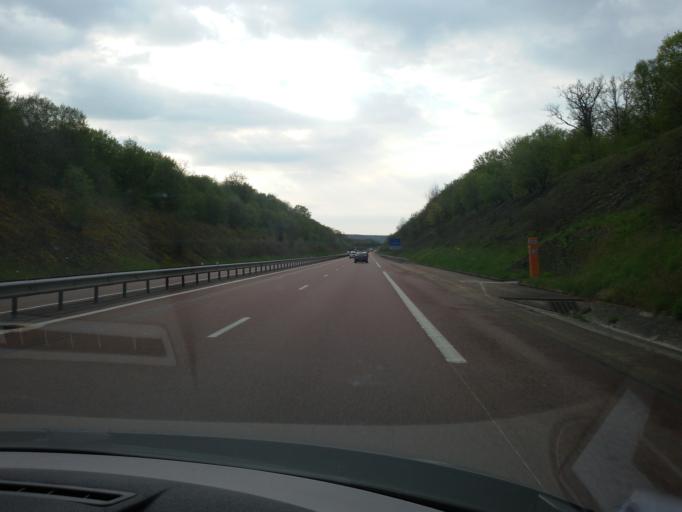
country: FR
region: Champagne-Ardenne
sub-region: Departement de la Haute-Marne
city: Chateauvillain
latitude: 48.0474
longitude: 4.9783
